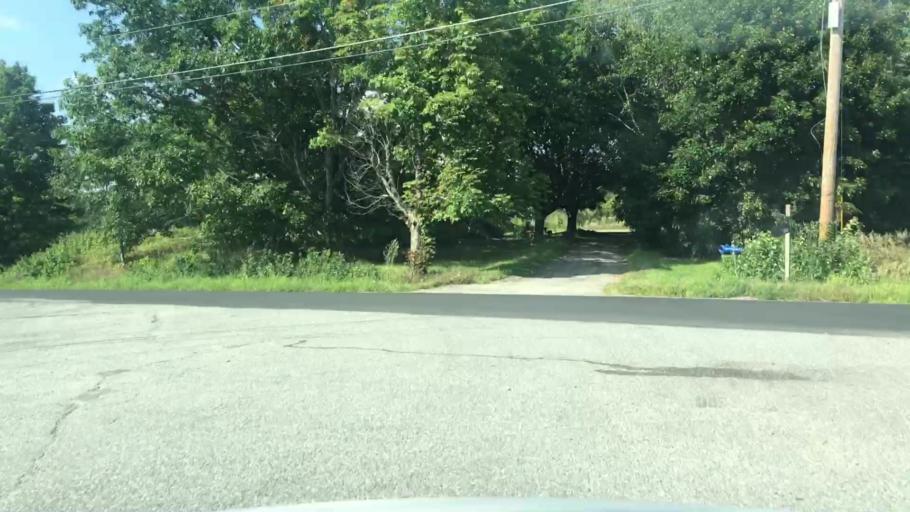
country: US
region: Maine
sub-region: Kennebec County
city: Waterville
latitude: 44.5785
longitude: -69.6672
